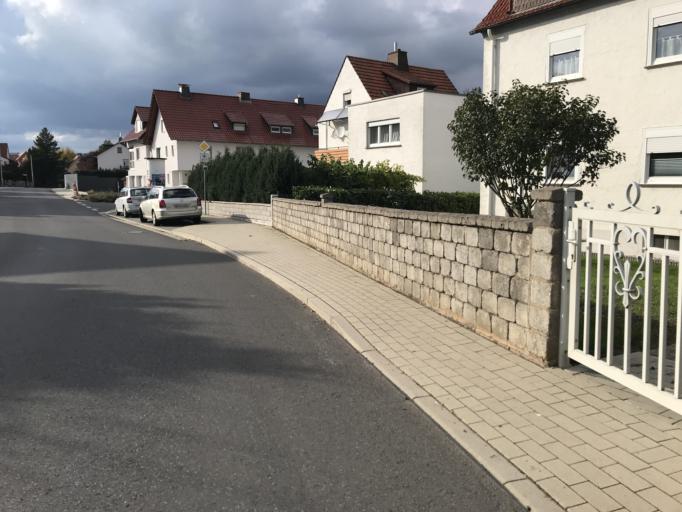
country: DE
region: Hesse
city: Borken
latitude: 51.0491
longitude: 9.2840
